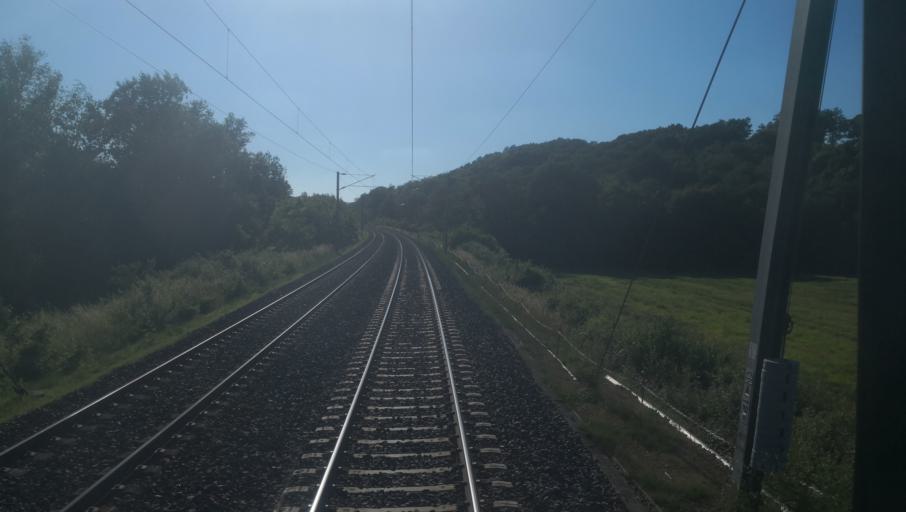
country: FR
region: Bourgogne
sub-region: Departement de la Nievre
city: Pouilly-sur-Loire
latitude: 47.3171
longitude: 2.8998
